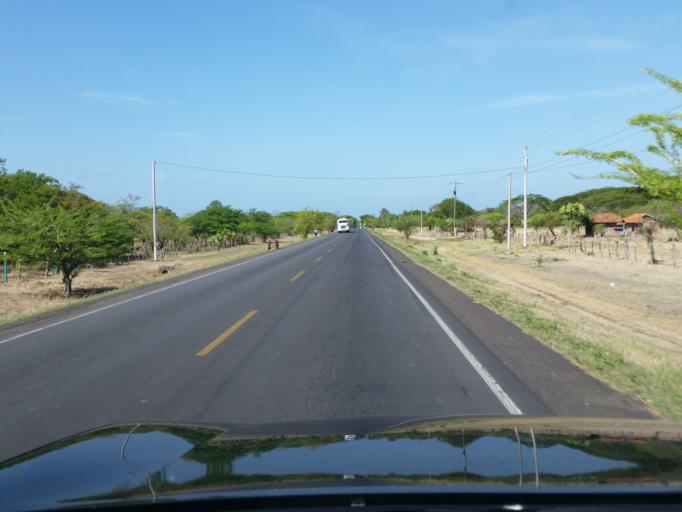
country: NI
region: Leon
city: La Paz Centro
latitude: 12.2981
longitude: -86.7123
